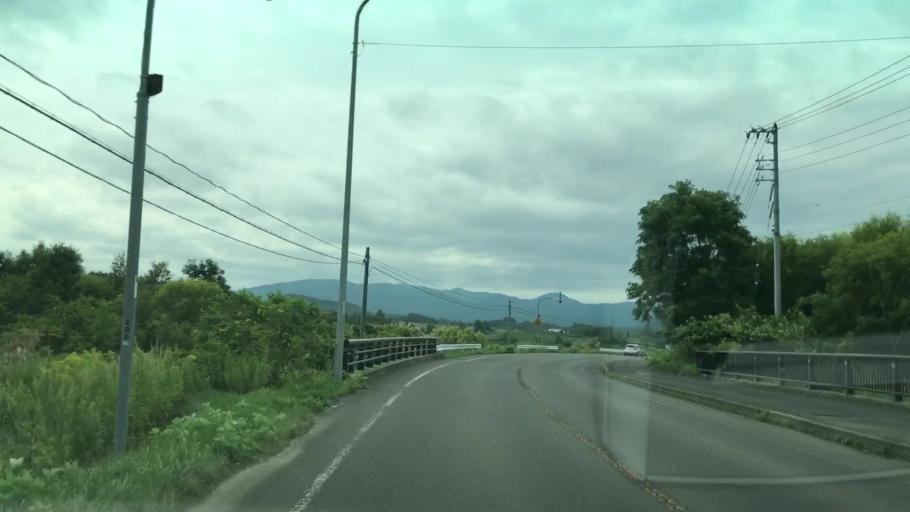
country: JP
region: Hokkaido
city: Yoichi
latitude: 43.1002
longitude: 140.8238
